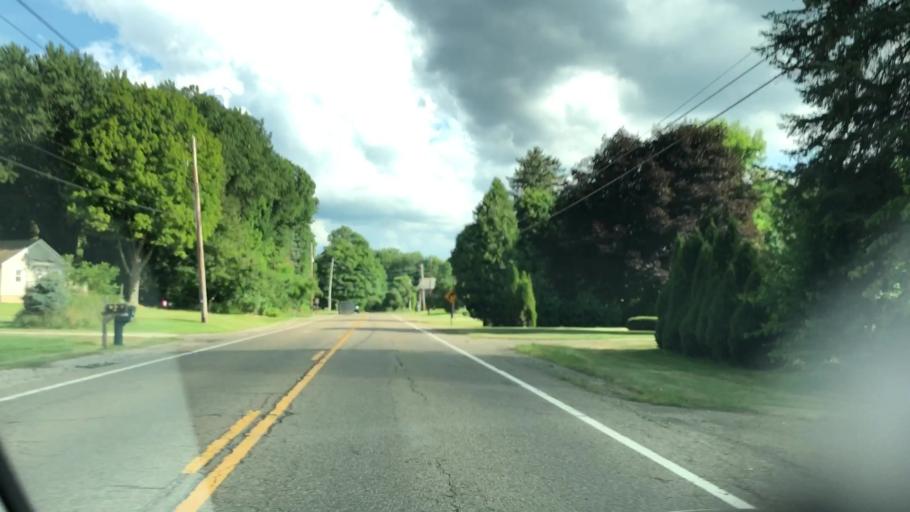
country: US
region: Ohio
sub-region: Summit County
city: Norton
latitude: 41.0761
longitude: -81.6399
